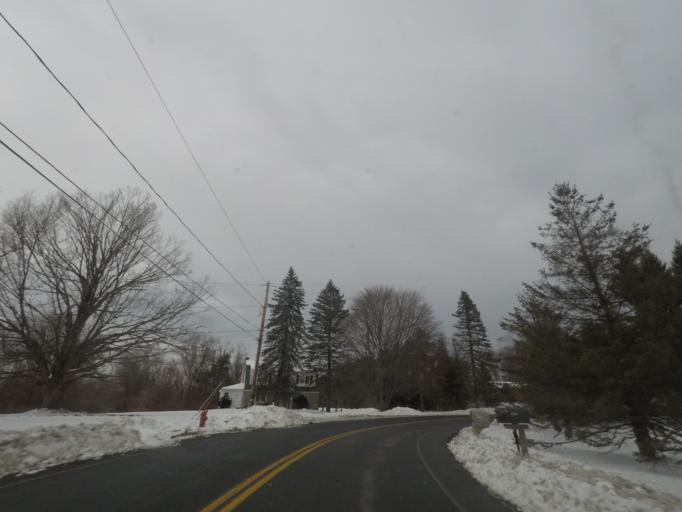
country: US
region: New York
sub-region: Rensselaer County
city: Castleton-on-Hudson
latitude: 42.5194
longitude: -73.6905
